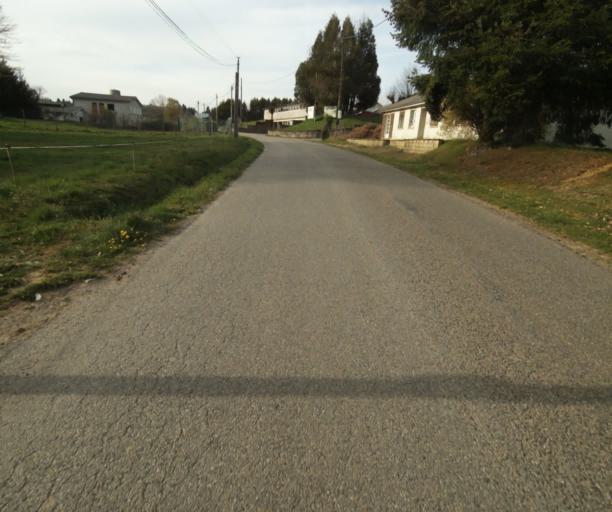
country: FR
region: Limousin
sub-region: Departement de la Correze
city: Naves
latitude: 45.3192
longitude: 1.7628
